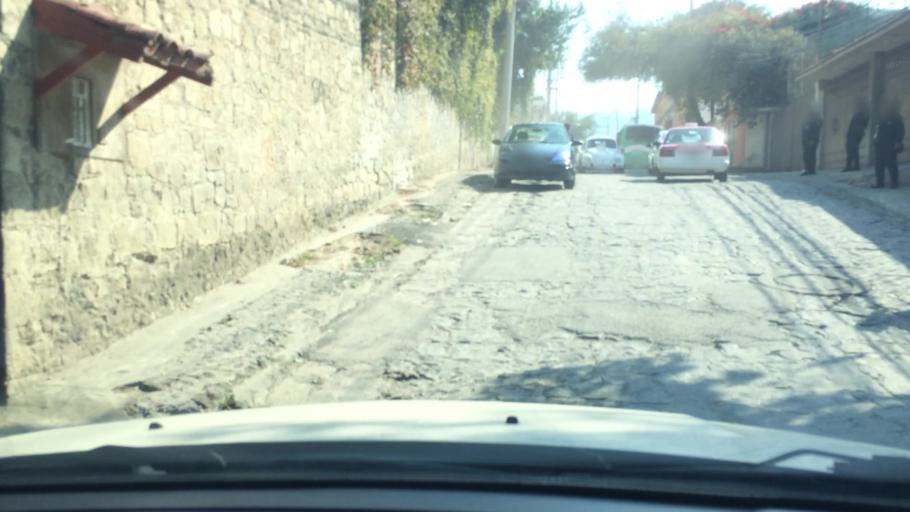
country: MX
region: Mexico City
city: Tlalpan
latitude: 19.2626
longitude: -99.1727
